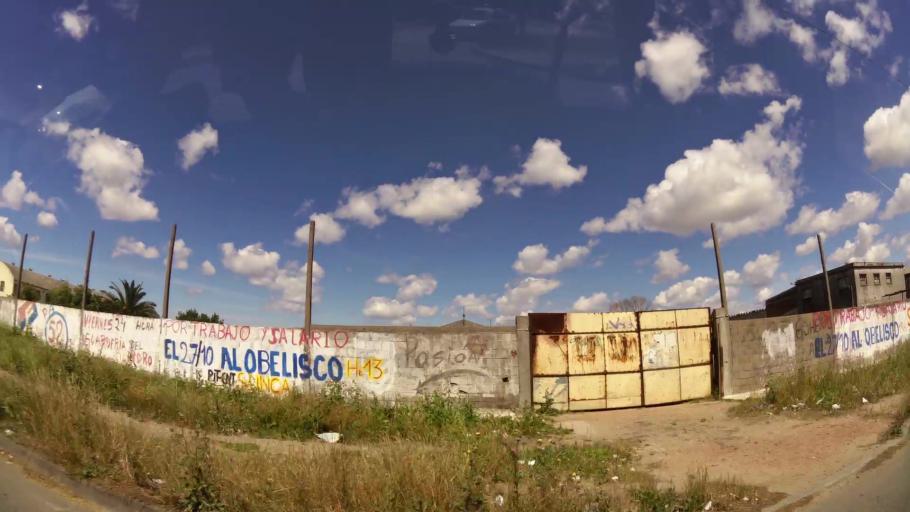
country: UY
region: Montevideo
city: Montevideo
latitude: -34.8440
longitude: -56.1359
